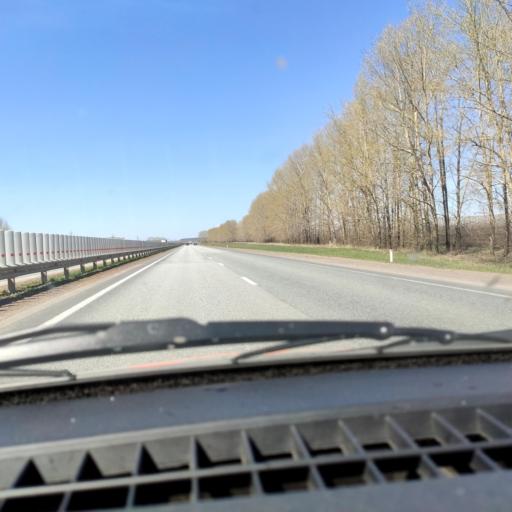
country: RU
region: Bashkortostan
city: Asanovo
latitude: 54.9892
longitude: 55.5174
